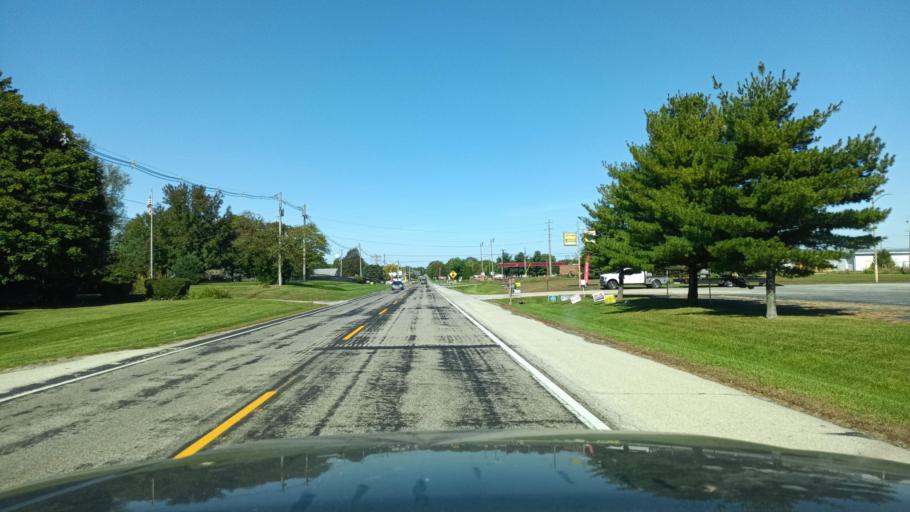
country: US
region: Illinois
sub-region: Champaign County
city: Lake of the Woods
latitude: 40.1943
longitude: -88.3653
